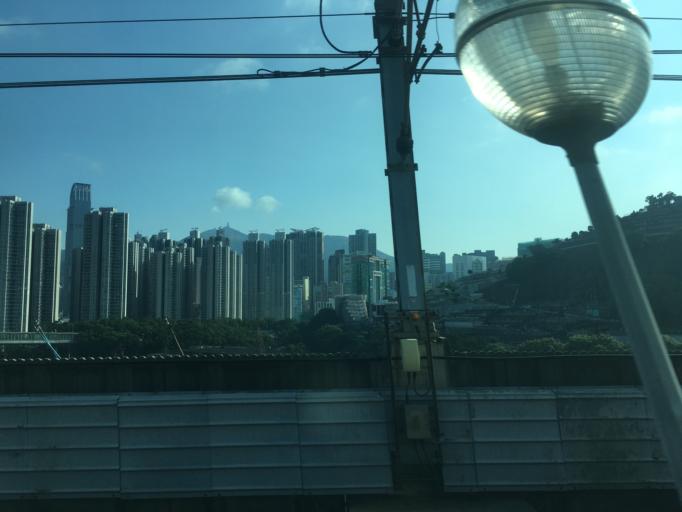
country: HK
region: Tsuen Wan
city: Tsuen Wan
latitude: 22.3564
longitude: 114.1137
